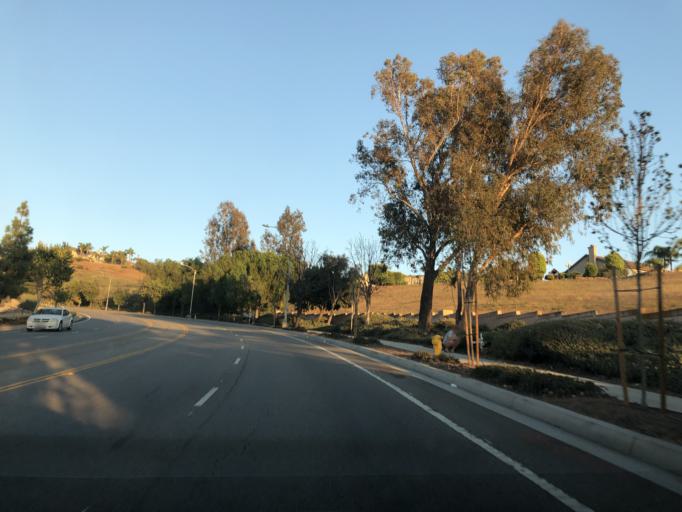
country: US
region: California
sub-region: Riverside County
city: Corona
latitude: 33.8968
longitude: -117.5522
